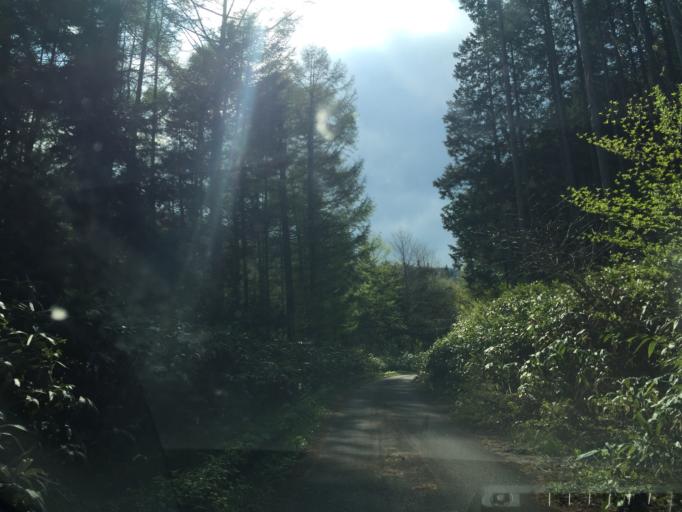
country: JP
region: Nagano
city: Iida
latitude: 35.5123
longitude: 137.6619
